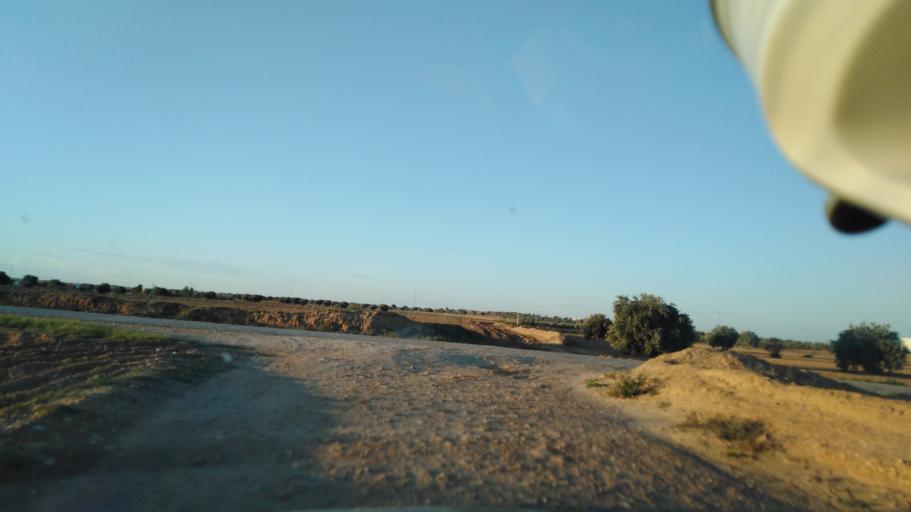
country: TN
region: Safaqis
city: Bi'r `Ali Bin Khalifah
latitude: 34.6739
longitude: 10.3829
